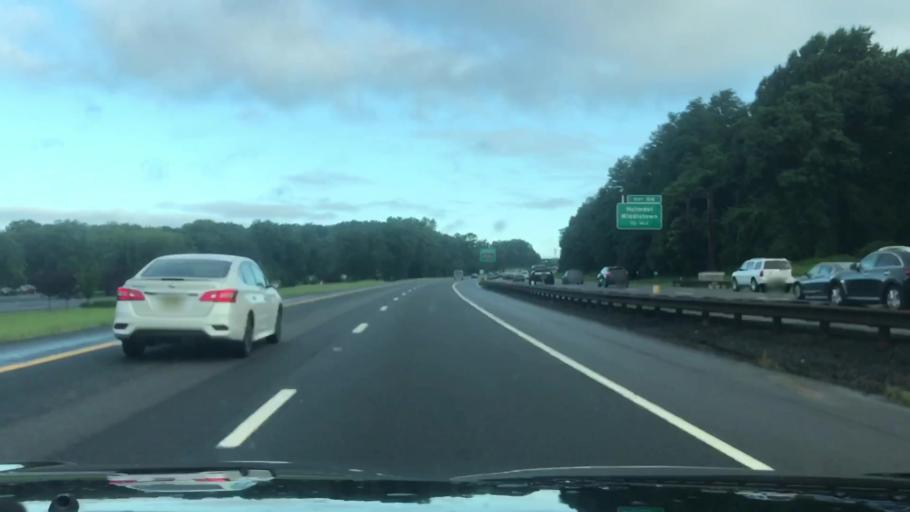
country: US
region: New Jersey
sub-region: Monmouth County
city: Lincroft
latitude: 40.3632
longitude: -74.1383
